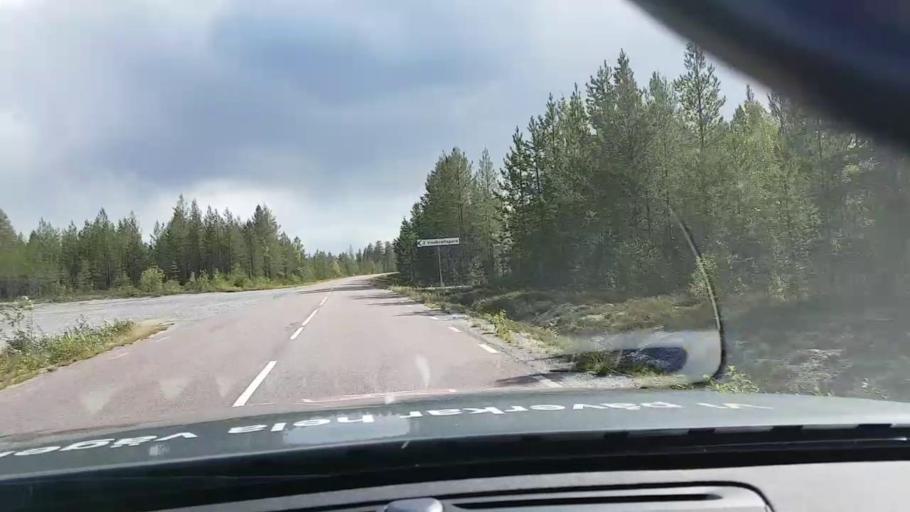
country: SE
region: Vaesterbotten
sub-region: Asele Kommun
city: Asele
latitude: 63.8872
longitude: 17.3507
